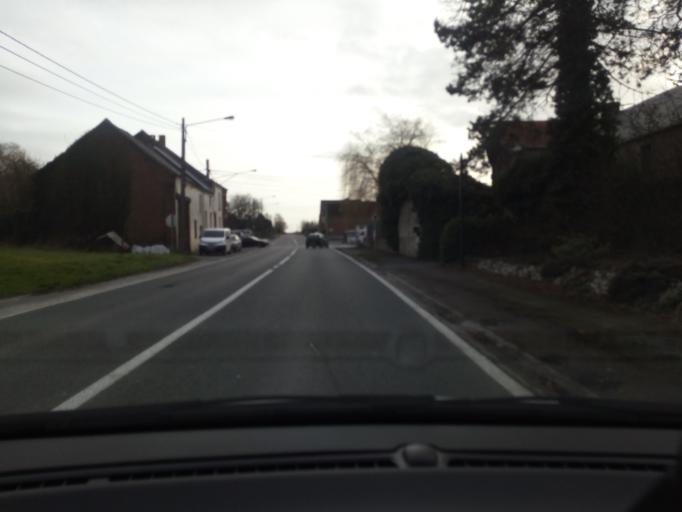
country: BE
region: Wallonia
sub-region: Province du Hainaut
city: Quevy-le-Petit
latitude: 50.3587
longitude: 3.8900
